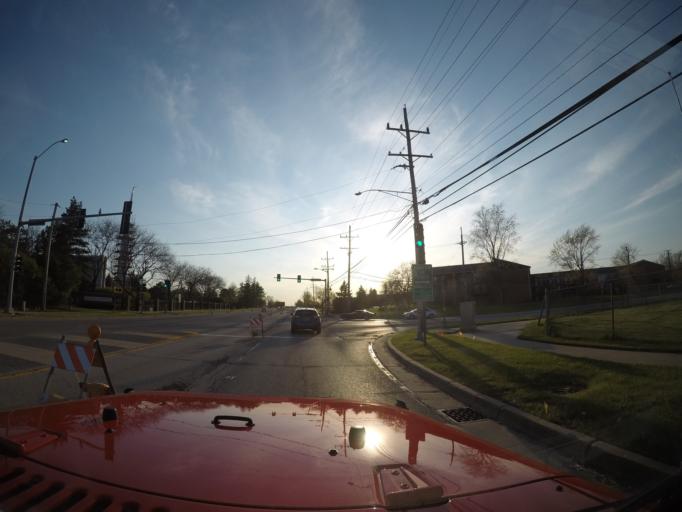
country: US
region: Illinois
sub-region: Cook County
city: Northbrook
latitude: 42.0877
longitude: -87.8590
